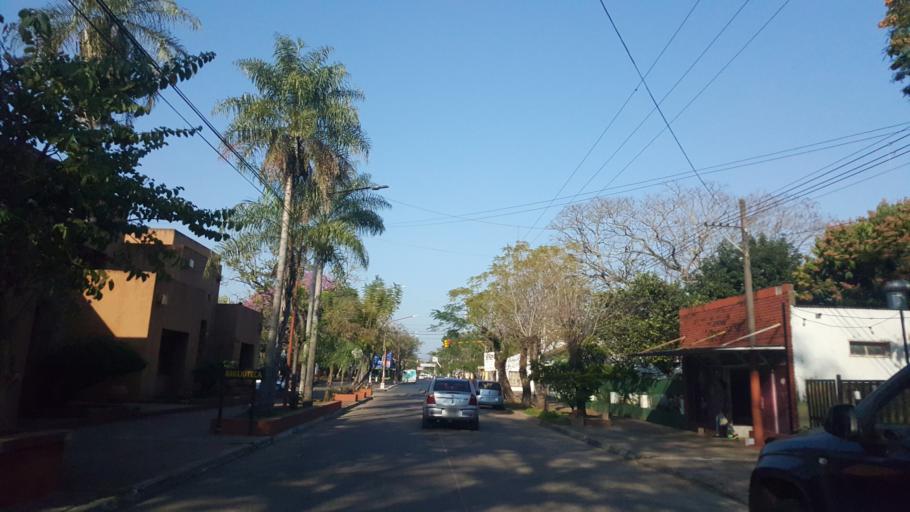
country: AR
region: Corrientes
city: Ituzaingo
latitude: -27.5840
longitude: -56.6866
